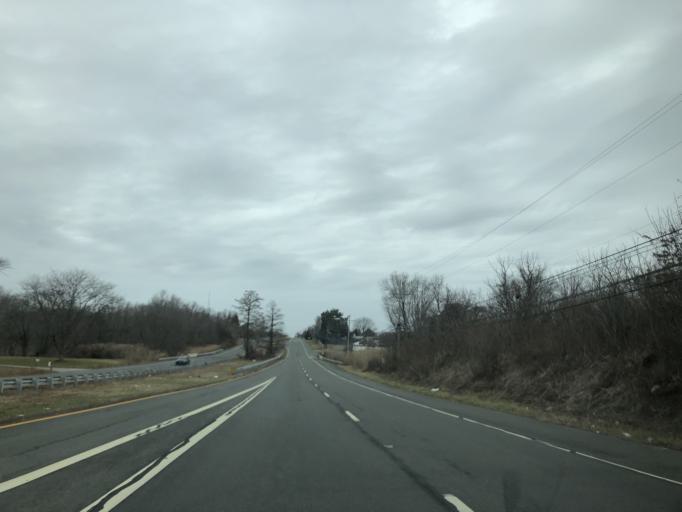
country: US
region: Delaware
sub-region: New Castle County
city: Bear
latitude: 39.5678
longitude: -75.6545
